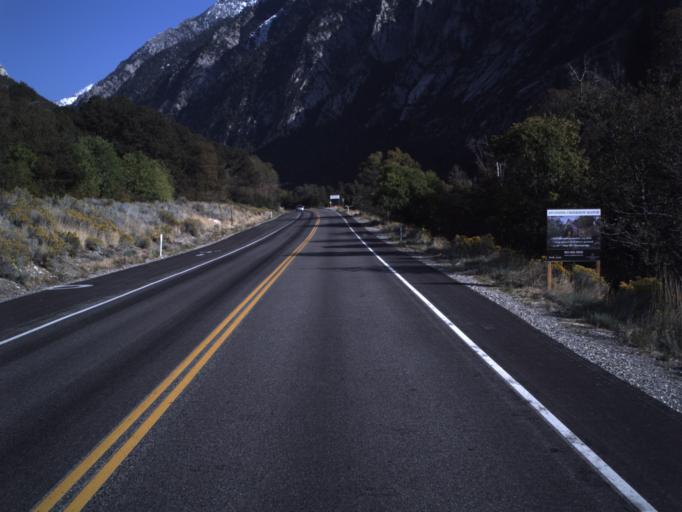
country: US
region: Utah
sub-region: Salt Lake County
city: Granite
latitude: 40.5754
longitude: -111.7836
